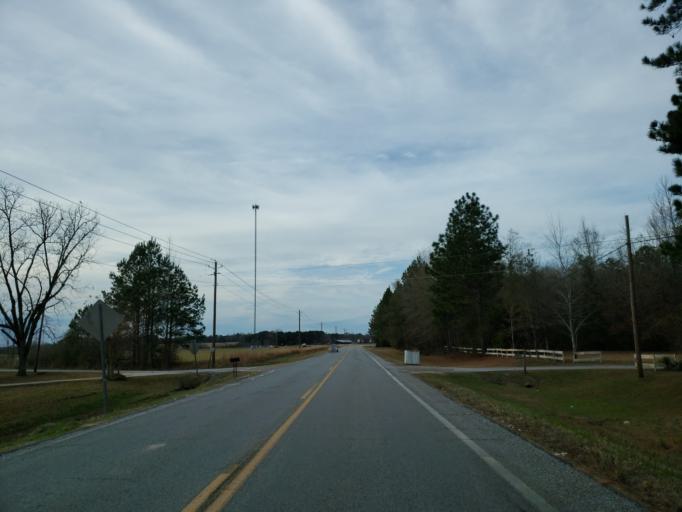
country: US
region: Mississippi
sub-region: Clarke County
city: Quitman
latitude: 31.8766
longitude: -88.7086
